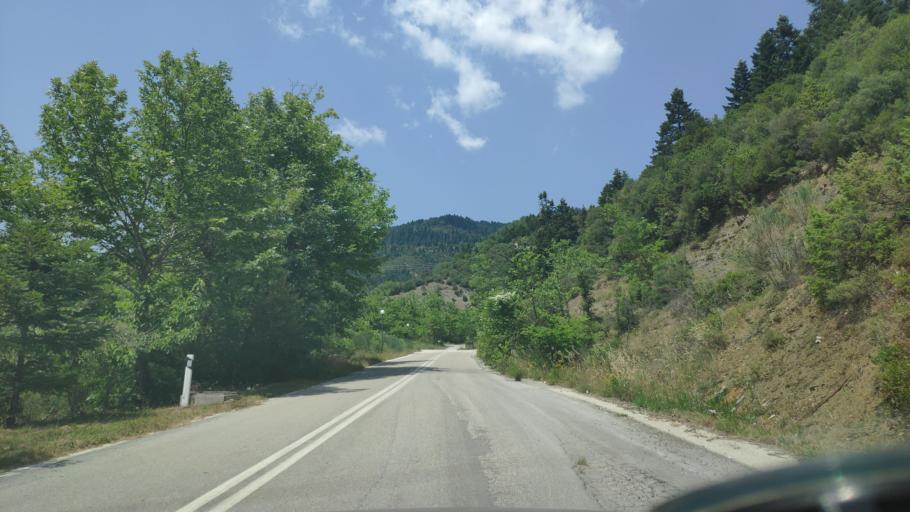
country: GR
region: Thessaly
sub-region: Nomos Kardhitsas
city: Anthiro
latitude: 39.2683
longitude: 21.3412
